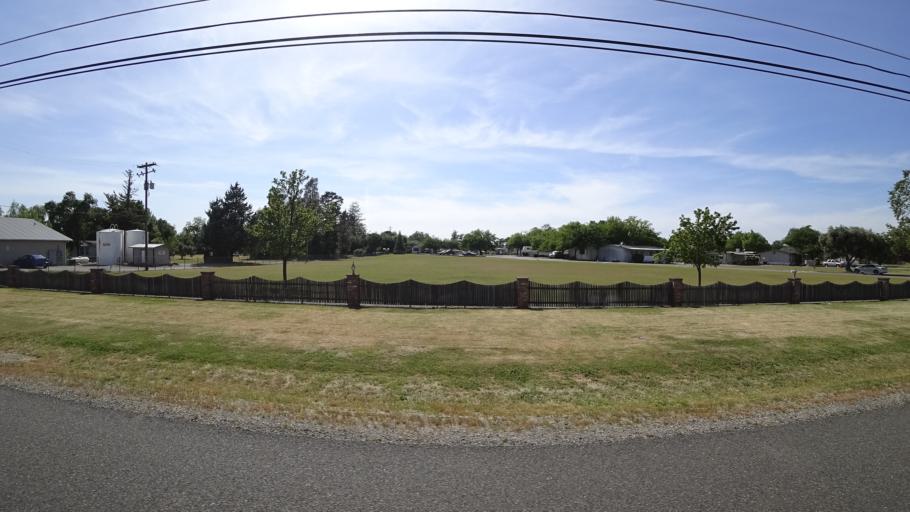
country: US
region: California
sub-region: Tehama County
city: Los Molinos
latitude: 40.0352
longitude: -122.0999
